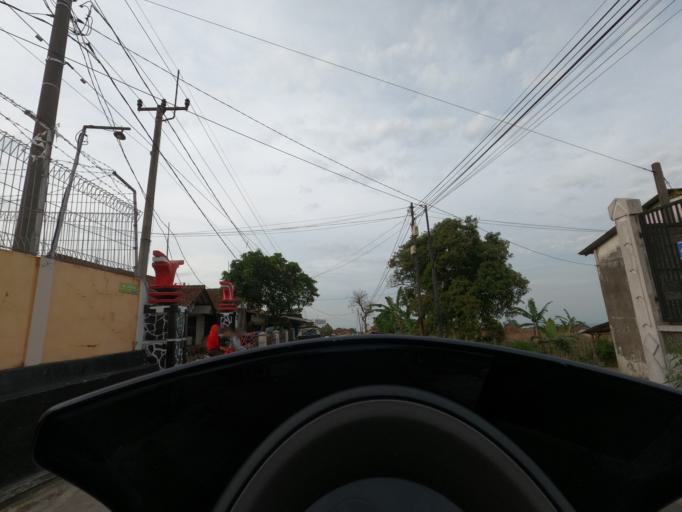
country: ID
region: West Java
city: Lembang
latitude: -6.7347
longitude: 107.6462
